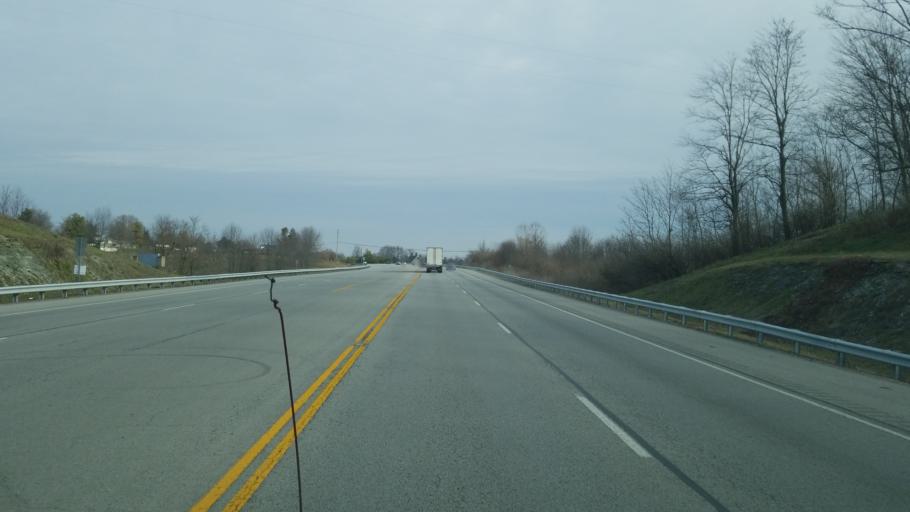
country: US
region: Kentucky
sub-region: Boyle County
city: Junction City
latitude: 37.5958
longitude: -84.7763
